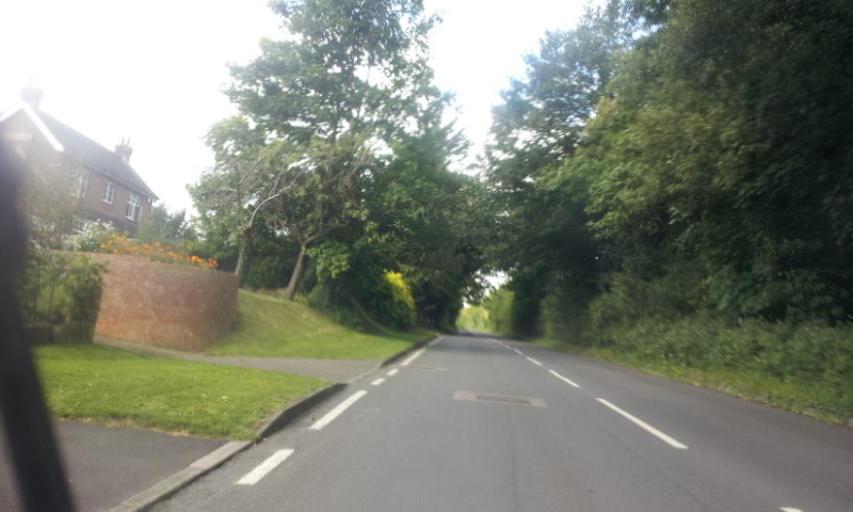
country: GB
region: England
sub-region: Kent
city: Larkfield
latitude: 51.2915
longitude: 0.4299
